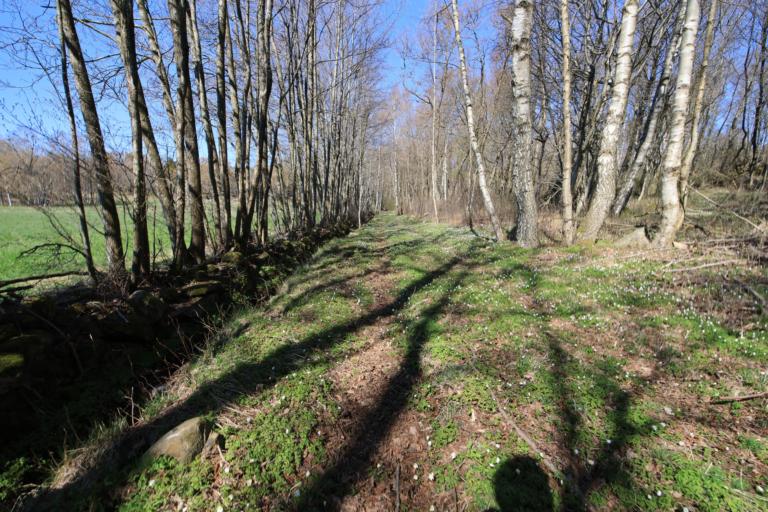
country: SE
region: Halland
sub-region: Varbergs Kommun
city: Varberg
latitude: 57.1635
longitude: 12.2525
